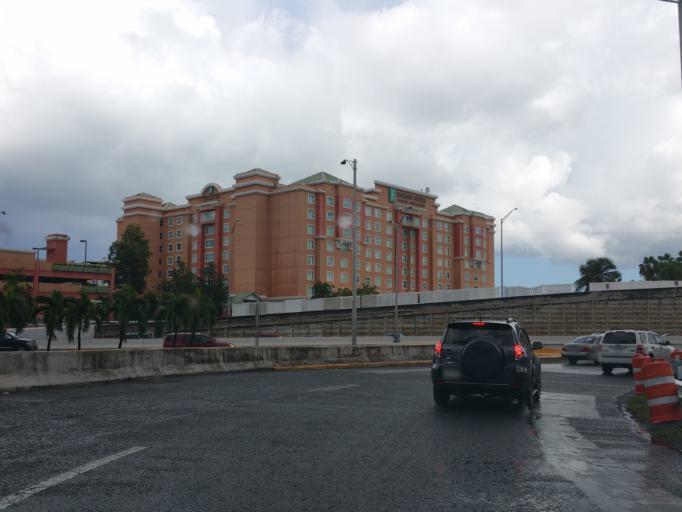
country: PR
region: Trujillo Alto
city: Trujillo Alto
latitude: 18.4386
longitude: -66.0237
